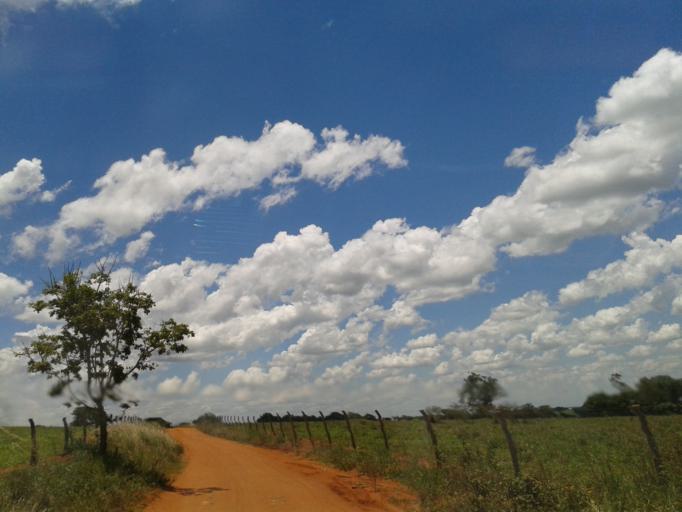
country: BR
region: Minas Gerais
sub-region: Centralina
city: Centralina
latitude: -18.7061
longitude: -49.1722
